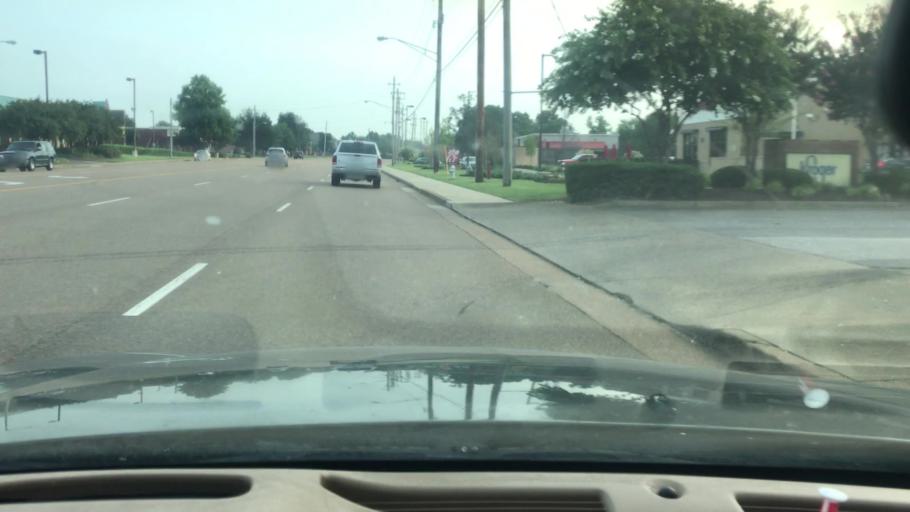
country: US
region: Tennessee
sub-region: Shelby County
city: Bartlett
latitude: 35.2061
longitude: -89.8405
